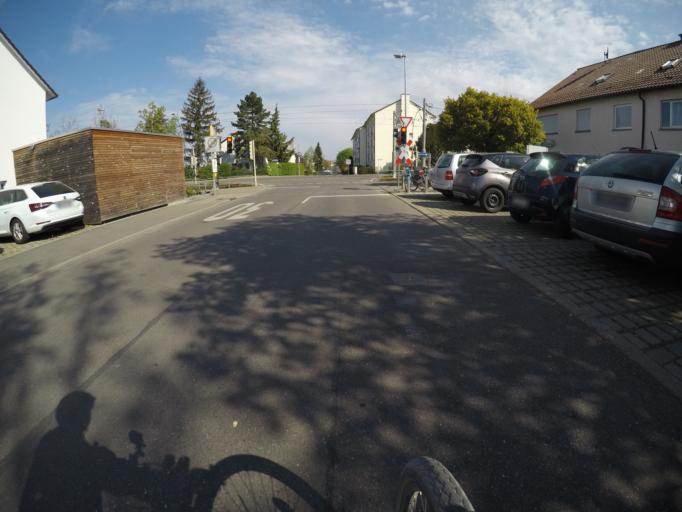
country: DE
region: Baden-Wuerttemberg
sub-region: Regierungsbezirk Stuttgart
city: Gerlingen
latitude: 48.8022
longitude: 9.0824
